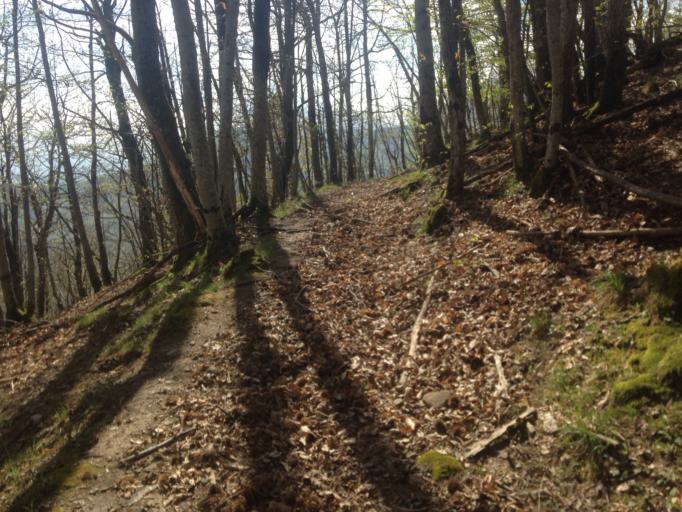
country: IT
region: Emilia-Romagna
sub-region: Provincia di Bologna
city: Lizzano in Belvedere
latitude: 44.1593
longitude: 10.8884
